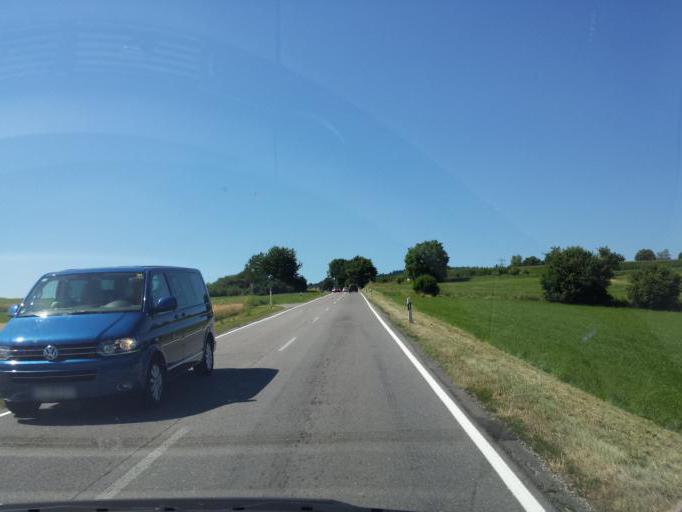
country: DE
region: Baden-Wuerttemberg
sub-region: Tuebingen Region
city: Owingen
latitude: 47.7859
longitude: 9.1710
